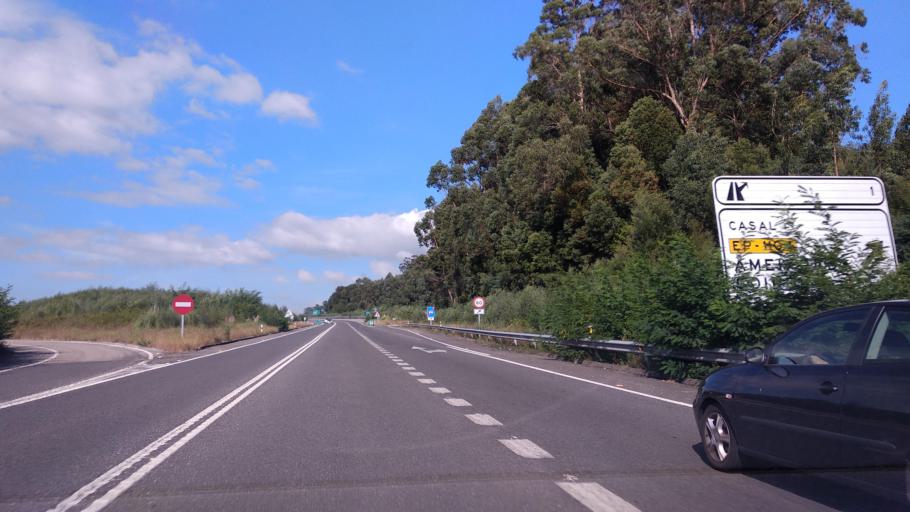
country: ES
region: Galicia
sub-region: Provincia de Pontevedra
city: Moana
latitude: 42.2758
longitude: -8.7557
